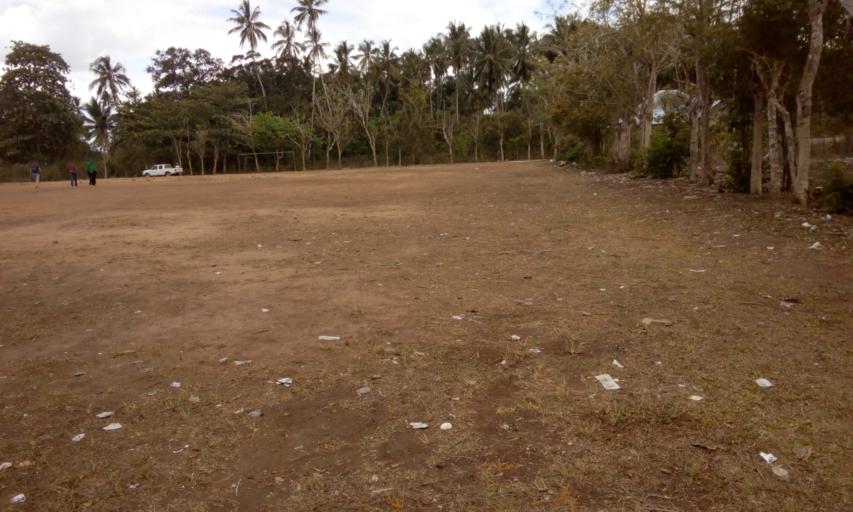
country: TZ
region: Zanzibar Central/South
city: Mahonda
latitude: -6.2965
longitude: 39.3722
